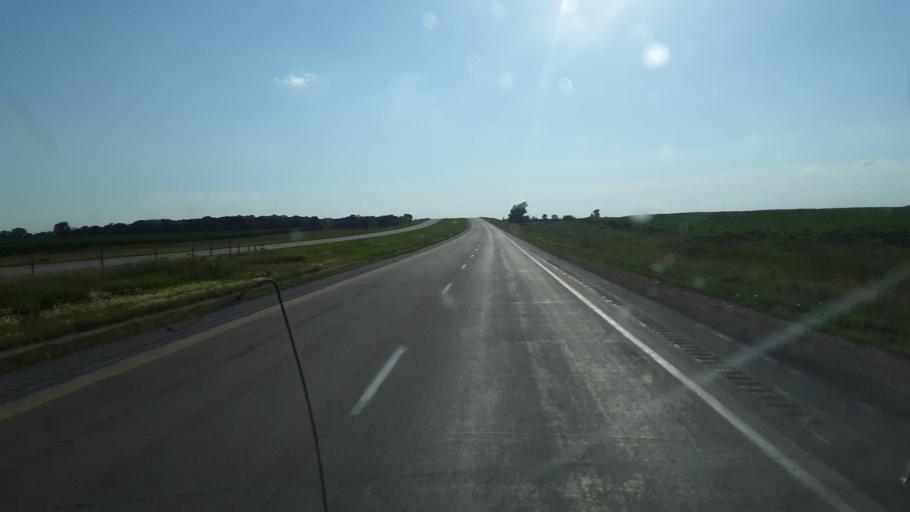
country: US
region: Iowa
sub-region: Hardin County
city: Iowa Falls
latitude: 42.4486
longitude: -93.3469
